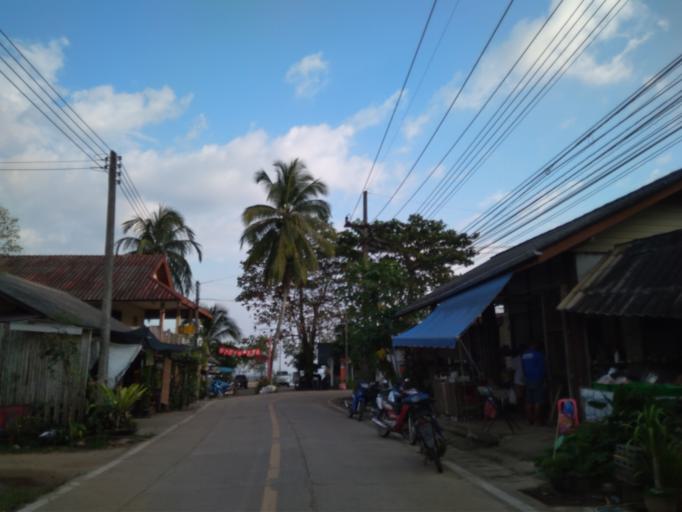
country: TH
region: Phangnga
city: Ko Yao
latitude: 8.1354
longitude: 98.6263
